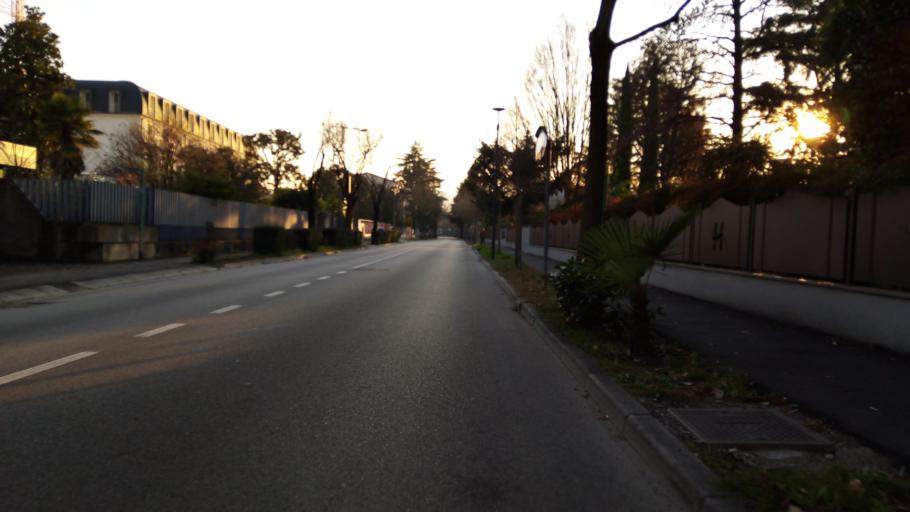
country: IT
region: Veneto
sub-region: Provincia di Padova
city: Abano Terme
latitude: 45.3482
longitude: 11.7774
